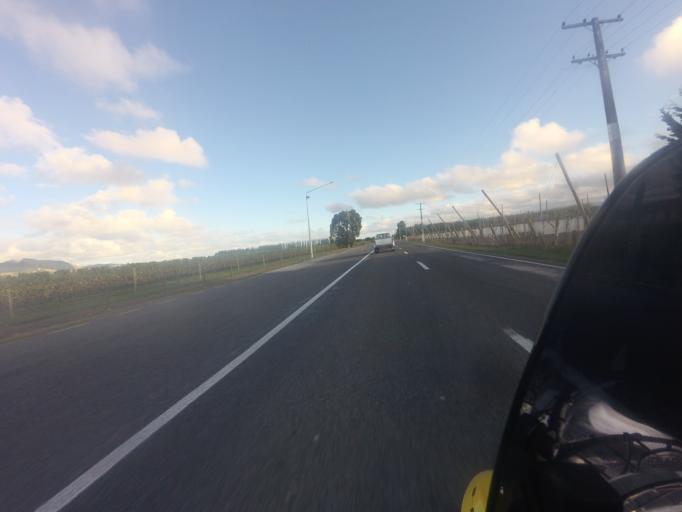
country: NZ
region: Gisborne
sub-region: Gisborne District
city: Gisborne
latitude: -38.5730
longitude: 177.9258
